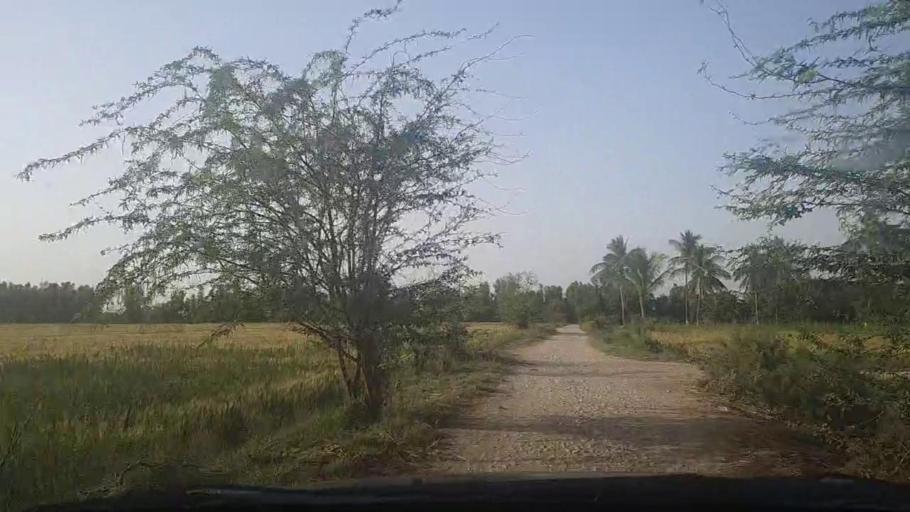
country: PK
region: Sindh
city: Keti Bandar
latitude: 24.2735
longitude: 67.5980
